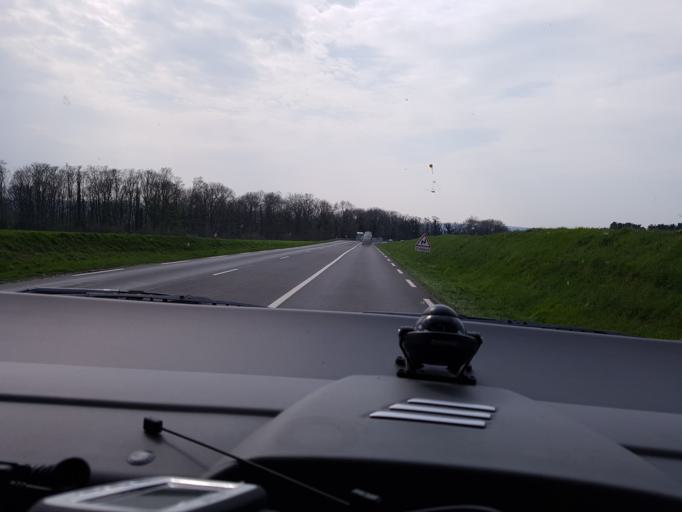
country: FR
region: Picardie
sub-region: Departement de l'Aisne
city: Crouy
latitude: 49.4114
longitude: 3.3413
